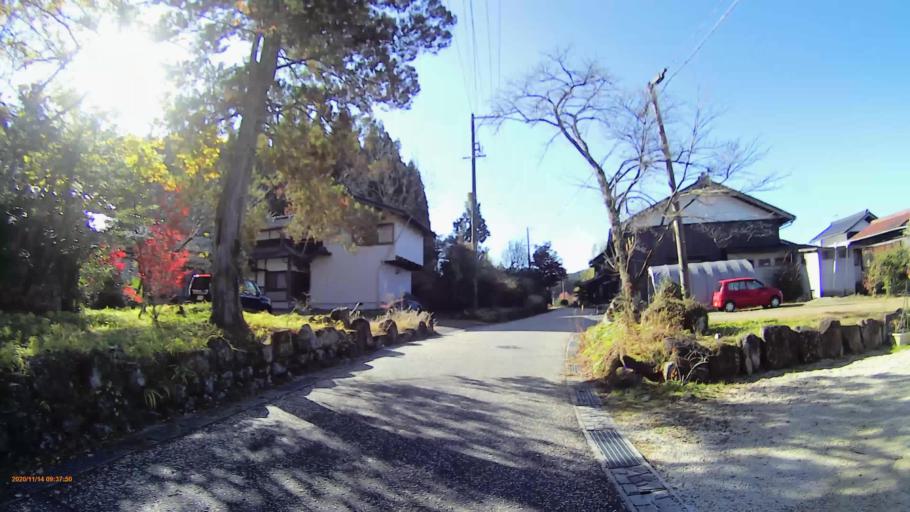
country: JP
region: Gifu
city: Nakatsugawa
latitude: 35.5207
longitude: 137.5613
